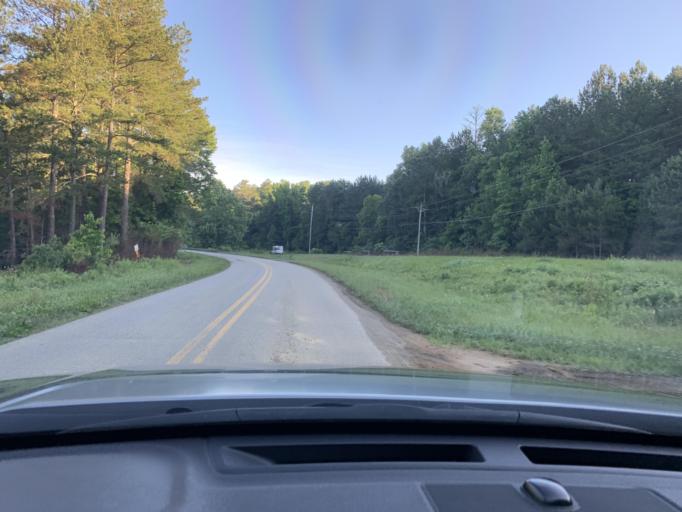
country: US
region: Georgia
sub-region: Bartow County
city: Rydal
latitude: 34.2529
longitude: -84.6878
